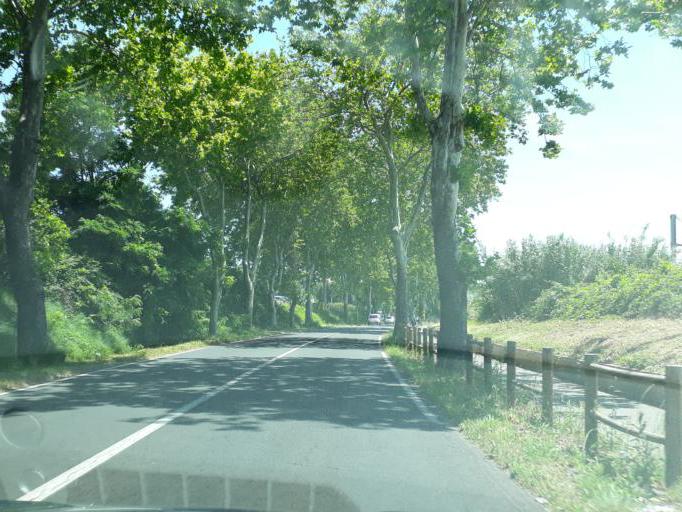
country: FR
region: Languedoc-Roussillon
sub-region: Departement de l'Herault
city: Beziers
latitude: 43.3307
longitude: 3.2396
